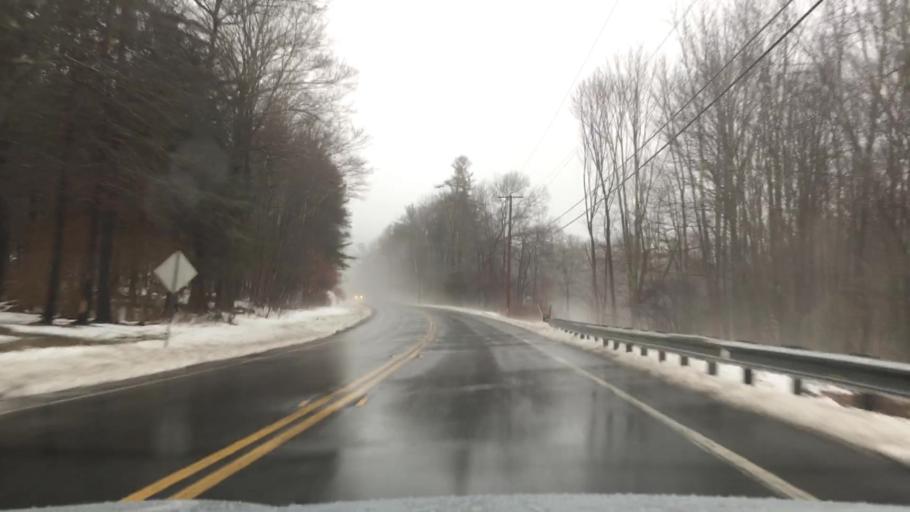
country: US
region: Massachusetts
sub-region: Hampshire County
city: Belchertown
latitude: 42.3298
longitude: -72.4016
